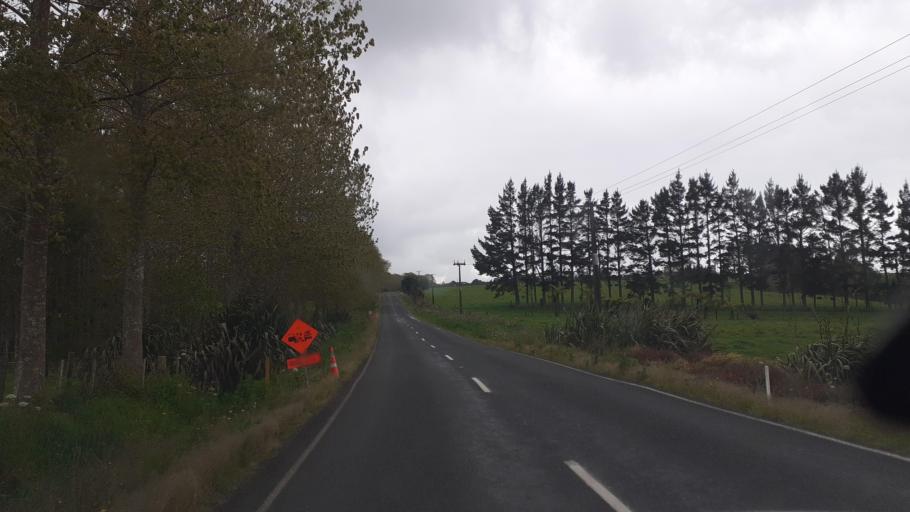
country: NZ
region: Northland
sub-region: Far North District
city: Waimate North
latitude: -35.2702
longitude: 173.8222
